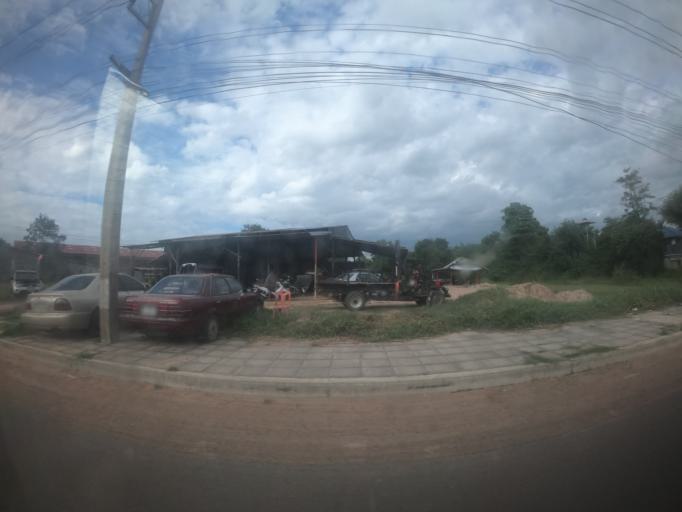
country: TH
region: Surin
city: Prasat
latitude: 14.6230
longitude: 103.4116
